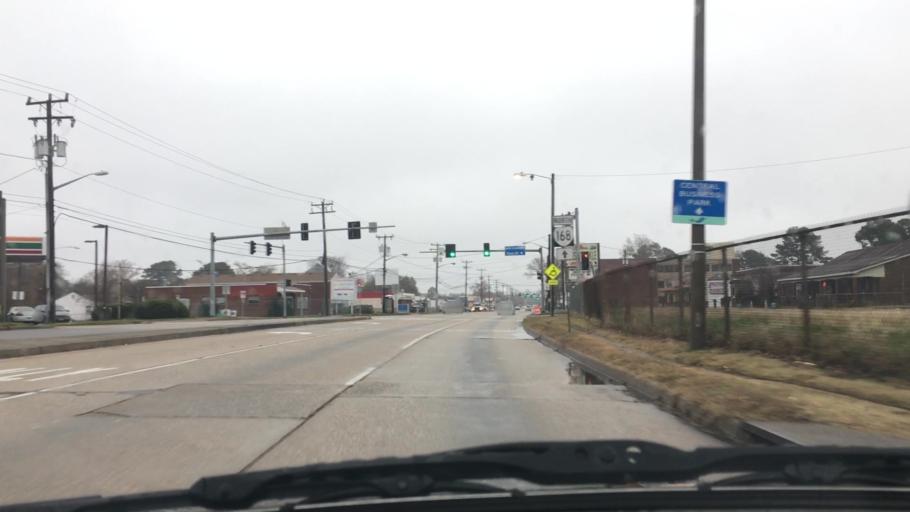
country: US
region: Virginia
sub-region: City of Norfolk
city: Norfolk
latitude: 36.9090
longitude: -76.2563
